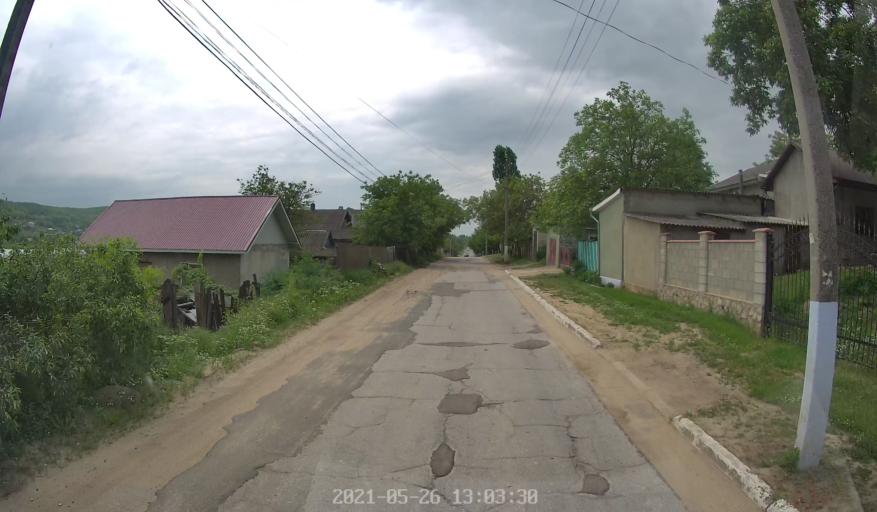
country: MD
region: Hincesti
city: Dancu
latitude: 46.7623
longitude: 28.3434
